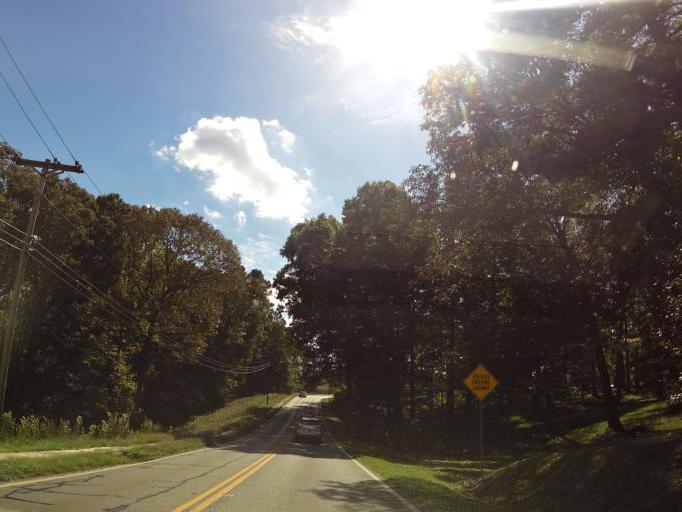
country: US
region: Georgia
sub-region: Pickens County
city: Nelson
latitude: 34.4158
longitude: -84.3853
